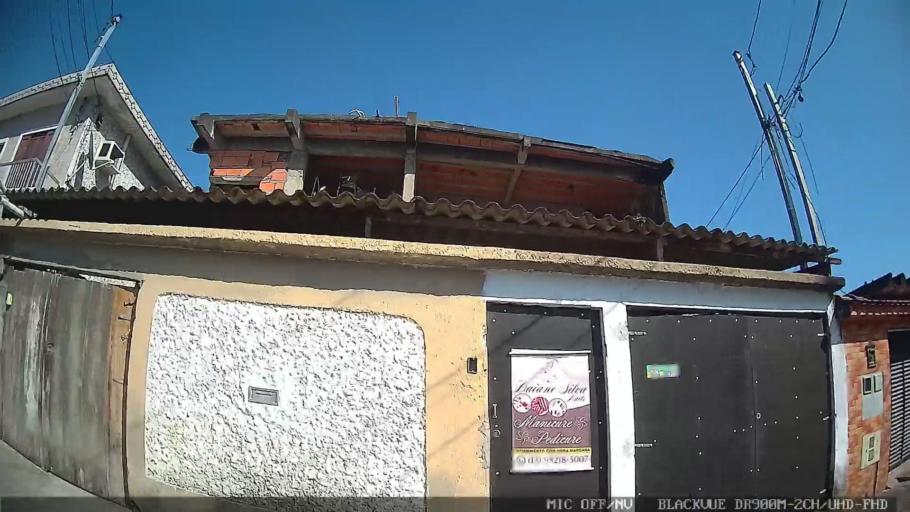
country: BR
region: Sao Paulo
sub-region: Santos
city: Santos
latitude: -23.9428
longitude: -46.2876
